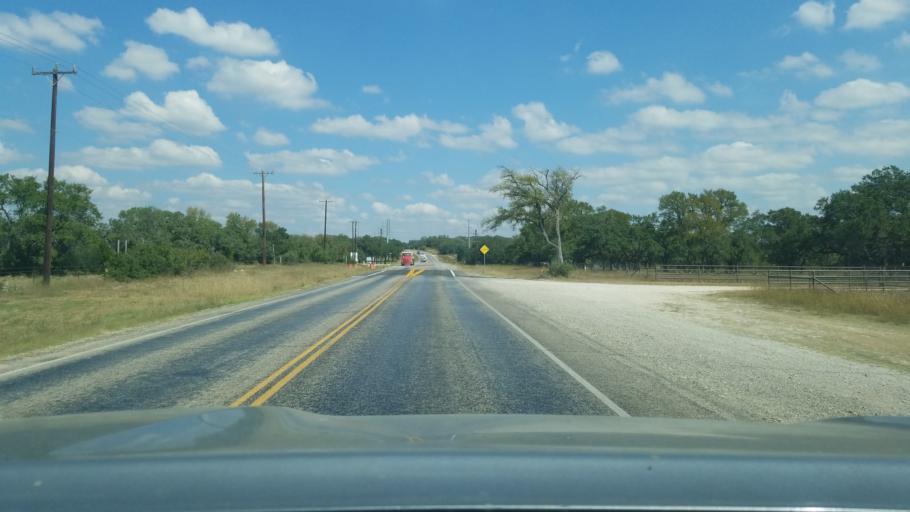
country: US
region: Texas
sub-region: Bexar County
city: Fair Oaks Ranch
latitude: 29.7591
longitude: -98.6146
